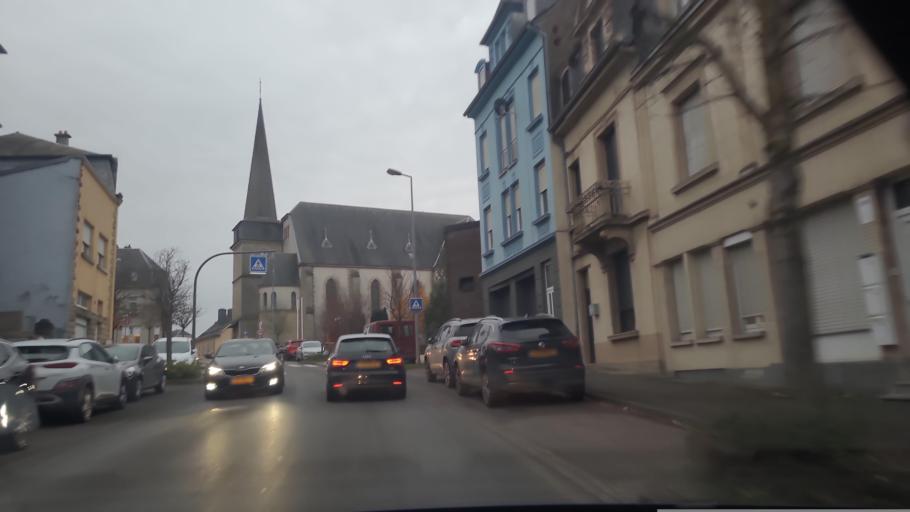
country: LU
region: Luxembourg
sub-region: Canton d'Esch-sur-Alzette
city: Obercorn
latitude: 49.5155
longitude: 5.8943
